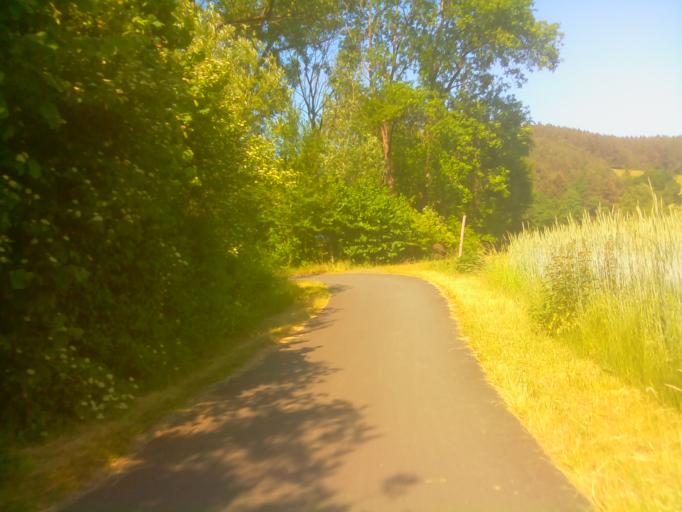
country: DE
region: Thuringia
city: Freienorla
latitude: 50.7528
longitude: 11.5501
